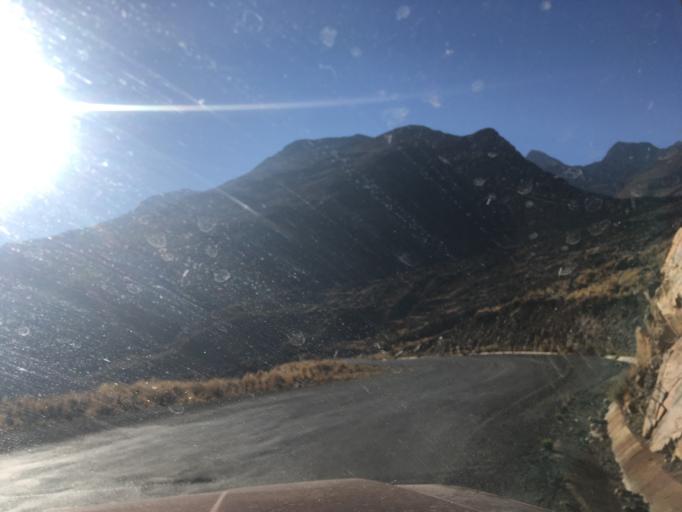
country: BO
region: La Paz
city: Quime
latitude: -17.0277
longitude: -67.2865
